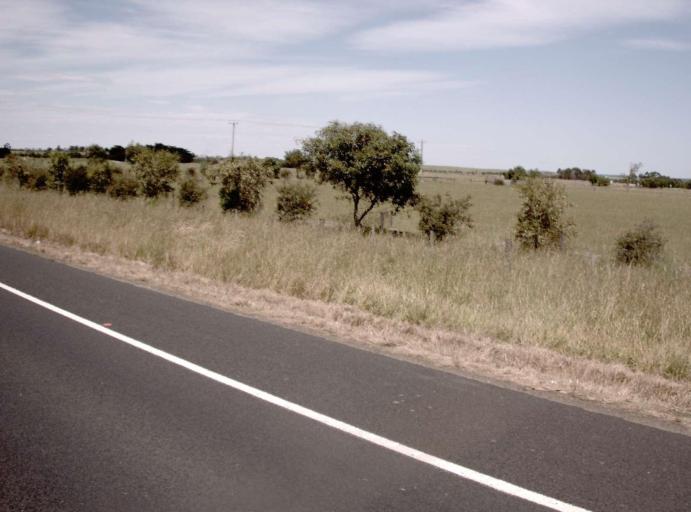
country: AU
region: Victoria
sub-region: Wellington
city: Heyfield
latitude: -38.1096
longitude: 146.8908
